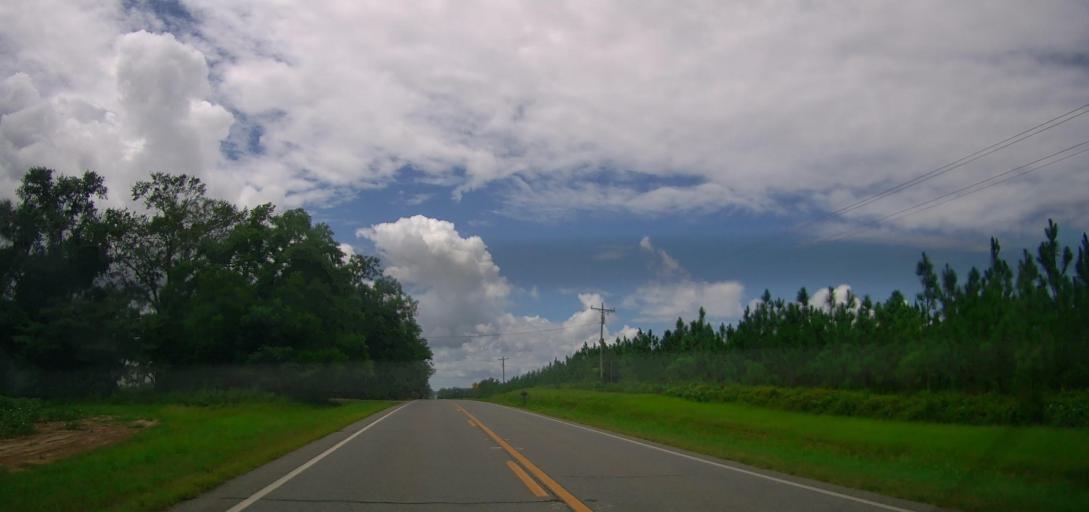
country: US
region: Georgia
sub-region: Wilcox County
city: Rochelle
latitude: 32.0358
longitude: -83.5826
